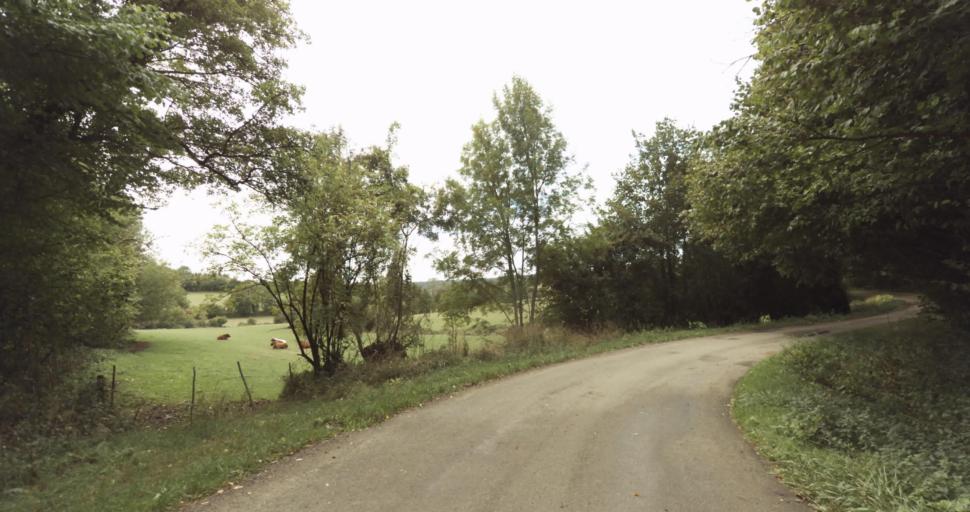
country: FR
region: Lower Normandy
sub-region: Departement de l'Orne
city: Gace
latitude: 48.7687
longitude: 0.3692
